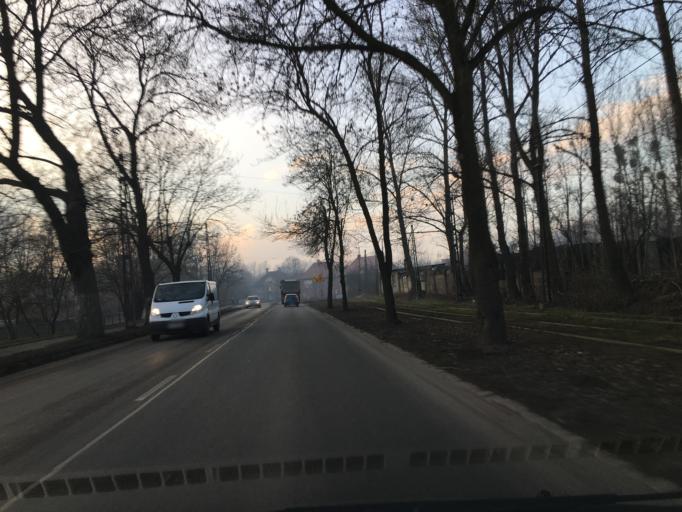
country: PL
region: Silesian Voivodeship
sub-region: Bytom
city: Bytom
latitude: 50.3390
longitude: 18.8763
